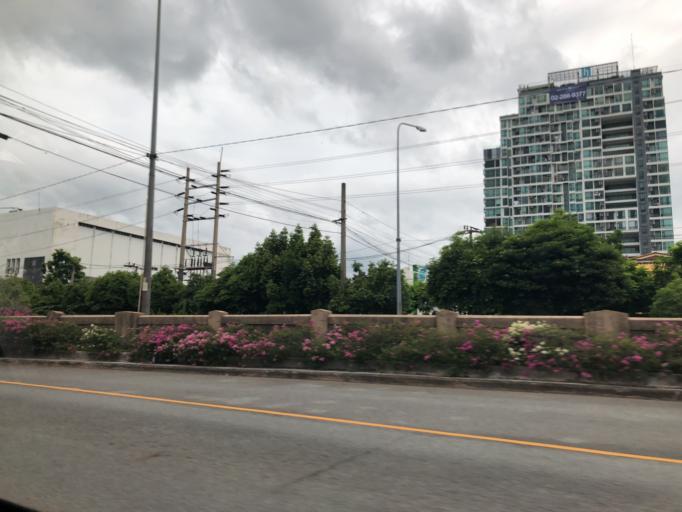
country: TH
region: Bangkok
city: Sathon
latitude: 13.7143
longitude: 100.5342
